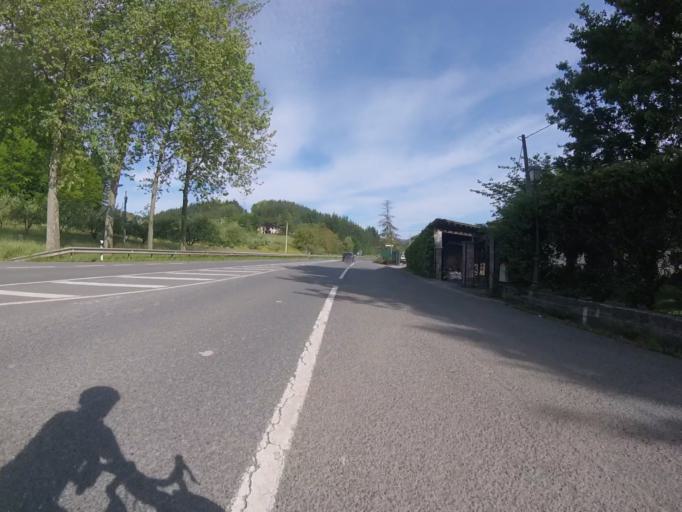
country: ES
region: Basque Country
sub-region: Provincia de Guipuzcoa
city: Ormaiztegui
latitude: 43.0547
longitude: -2.2655
